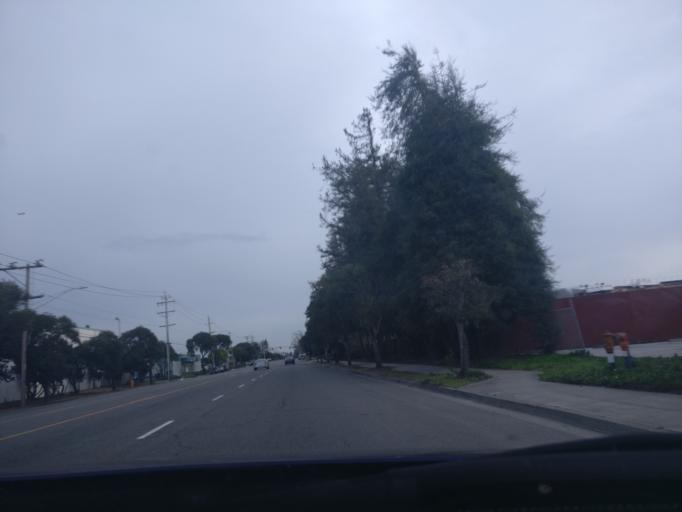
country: US
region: California
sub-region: Alameda County
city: San Lorenzo
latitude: 37.6525
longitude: -122.1204
